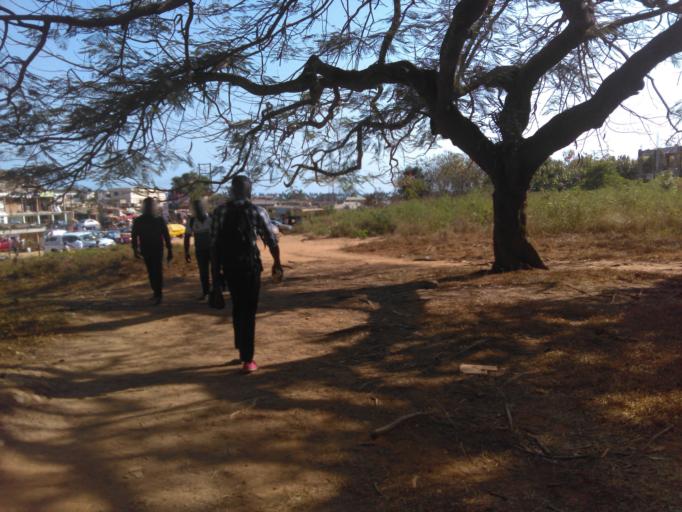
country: GH
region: Central
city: Cape Coast
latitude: 5.1154
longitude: -1.2934
